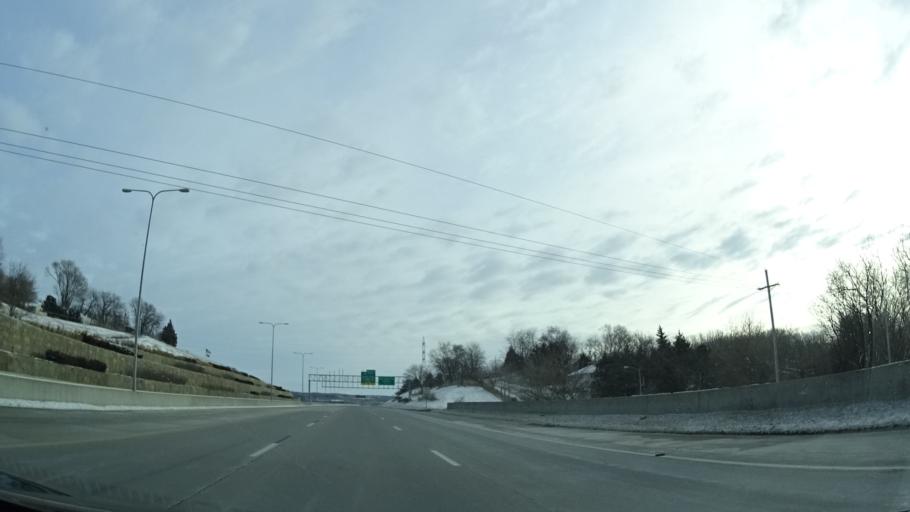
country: US
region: Nebraska
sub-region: Douglas County
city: Omaha
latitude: 41.2308
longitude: -95.9225
